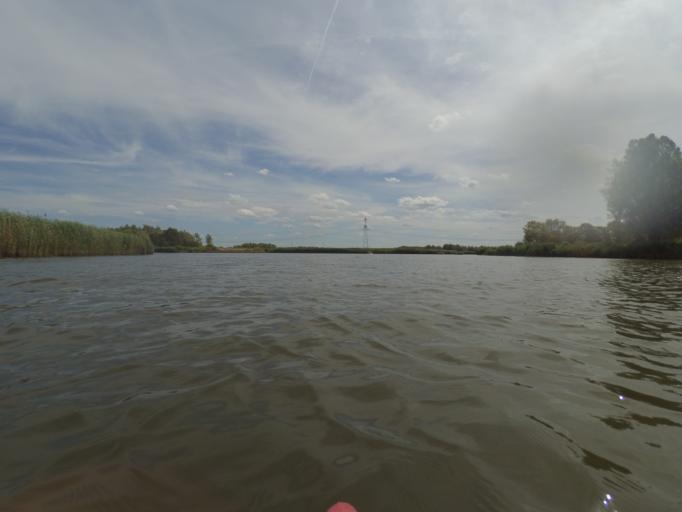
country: NL
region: North Brabant
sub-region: Gemeente Geertruidenberg
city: Geertruidenberg
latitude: 51.7259
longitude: 4.8508
